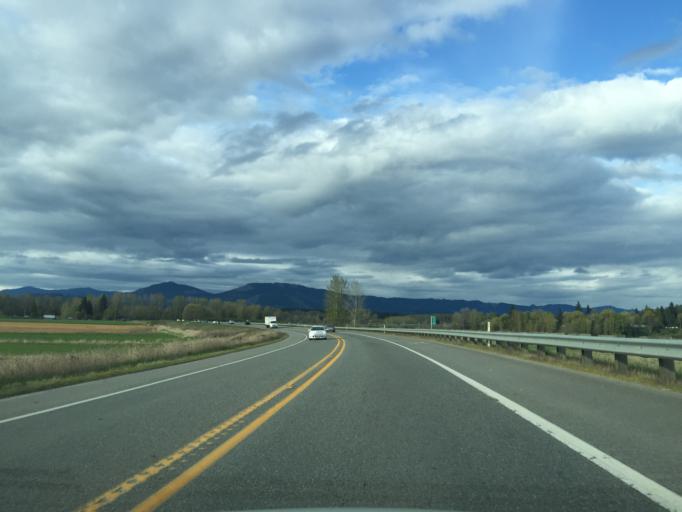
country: US
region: Washington
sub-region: Snohomish County
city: Arlington
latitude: 48.1905
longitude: -122.1403
